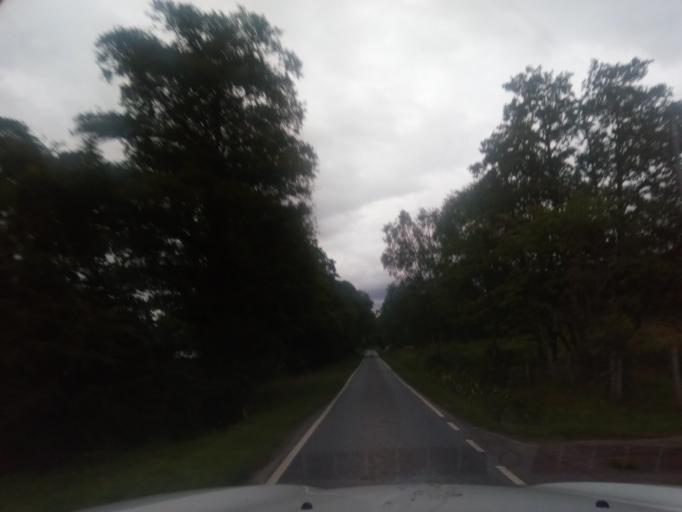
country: GB
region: Scotland
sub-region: Highland
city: Fort William
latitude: 56.8466
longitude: -5.2853
